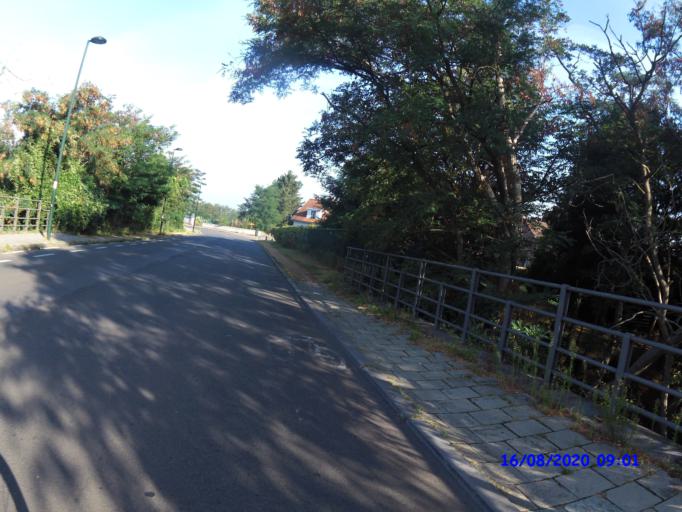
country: BE
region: Flanders
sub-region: Provincie Vlaams-Brabant
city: Linkebeek
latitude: 50.7801
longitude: 4.3346
